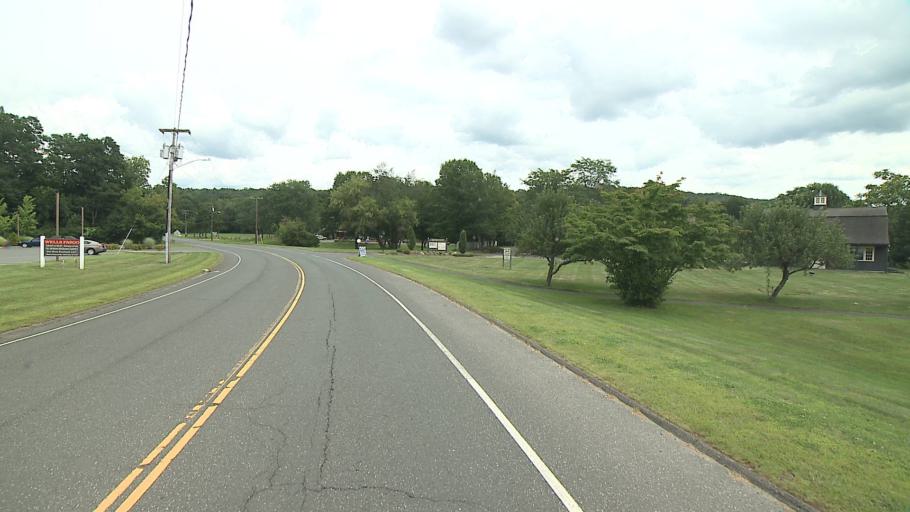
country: US
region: Connecticut
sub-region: Litchfield County
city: Woodbury Center
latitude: 41.5278
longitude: -73.2030
